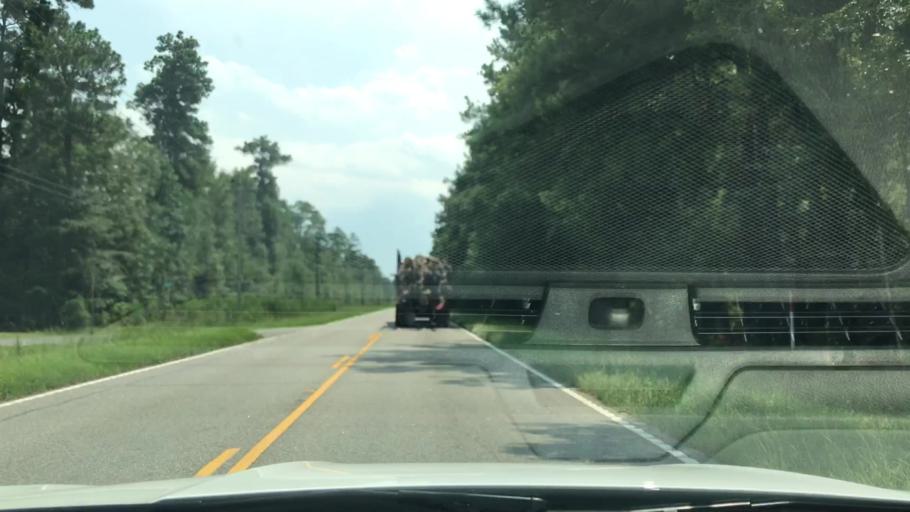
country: US
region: South Carolina
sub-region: Georgetown County
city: Georgetown
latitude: 33.4508
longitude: -79.2794
